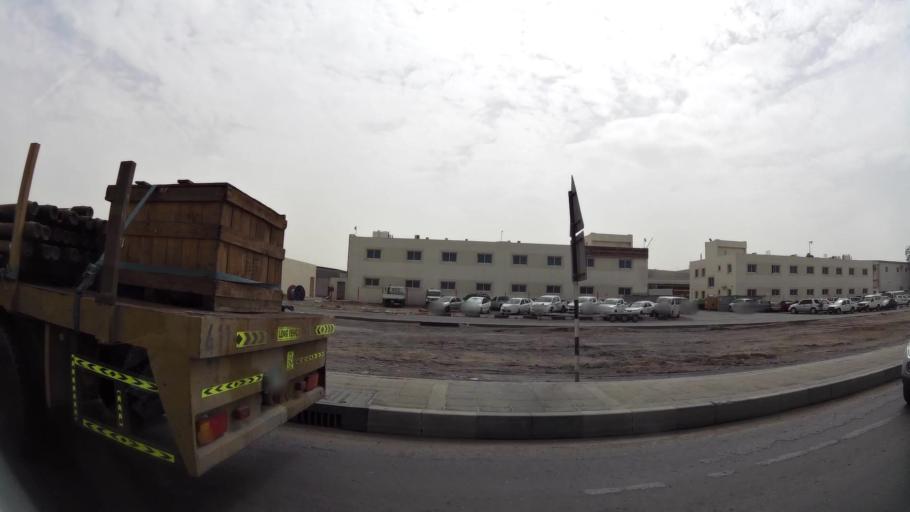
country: AE
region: Abu Dhabi
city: Abu Dhabi
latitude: 24.3464
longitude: 54.5108
